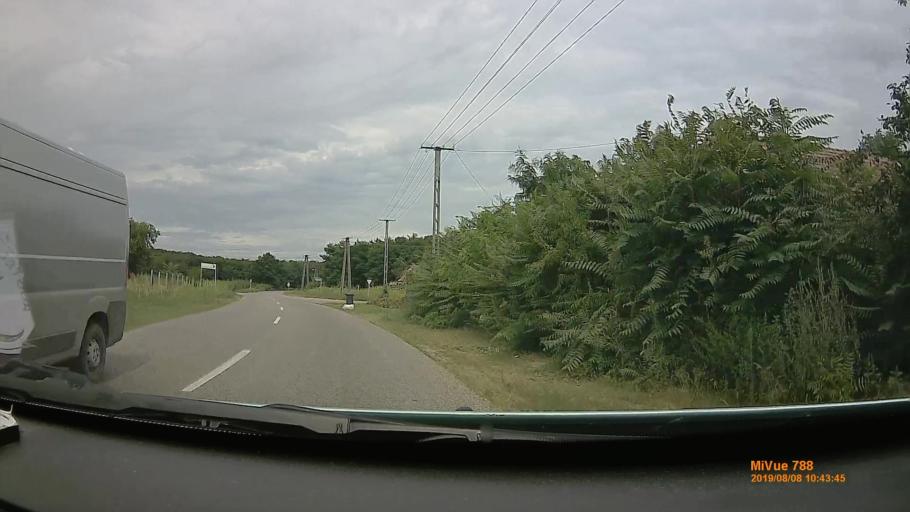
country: HU
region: Szabolcs-Szatmar-Bereg
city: Balkany
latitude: 47.7245
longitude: 21.8764
